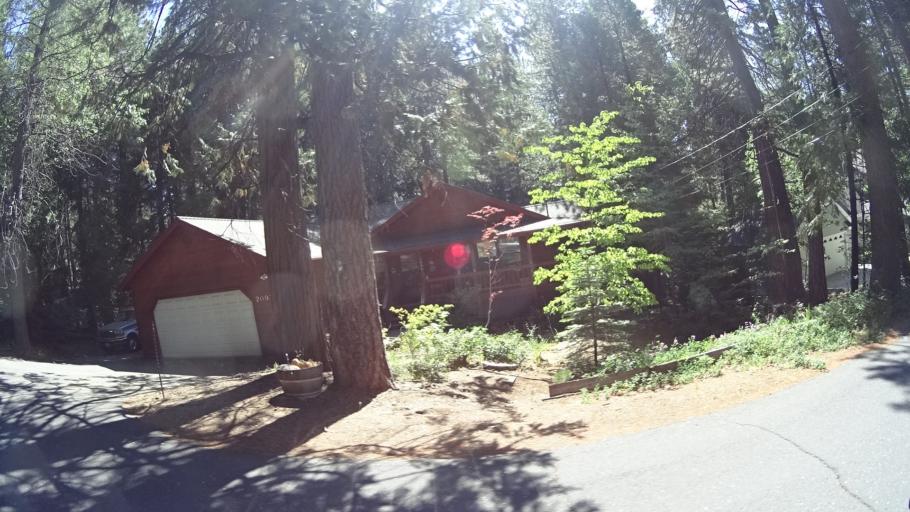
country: US
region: California
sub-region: Calaveras County
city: Arnold
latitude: 38.2516
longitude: -120.3628
